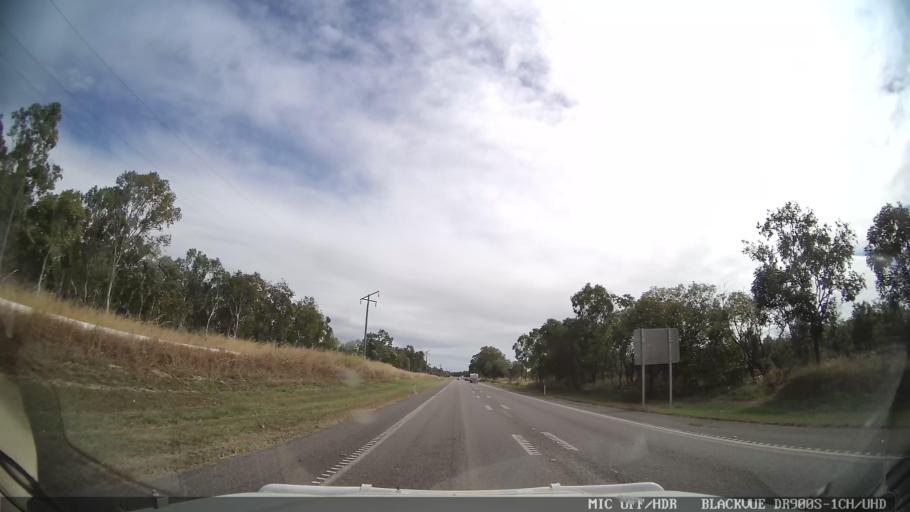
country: AU
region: Queensland
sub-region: Hinchinbrook
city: Ingham
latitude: -19.0053
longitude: 146.3592
